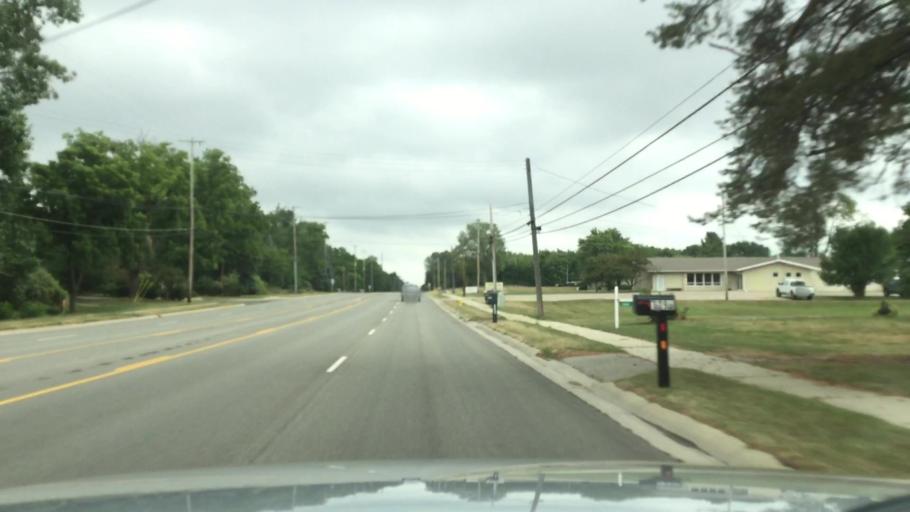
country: US
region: Michigan
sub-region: Genesee County
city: Davison
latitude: 43.0338
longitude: -83.5650
